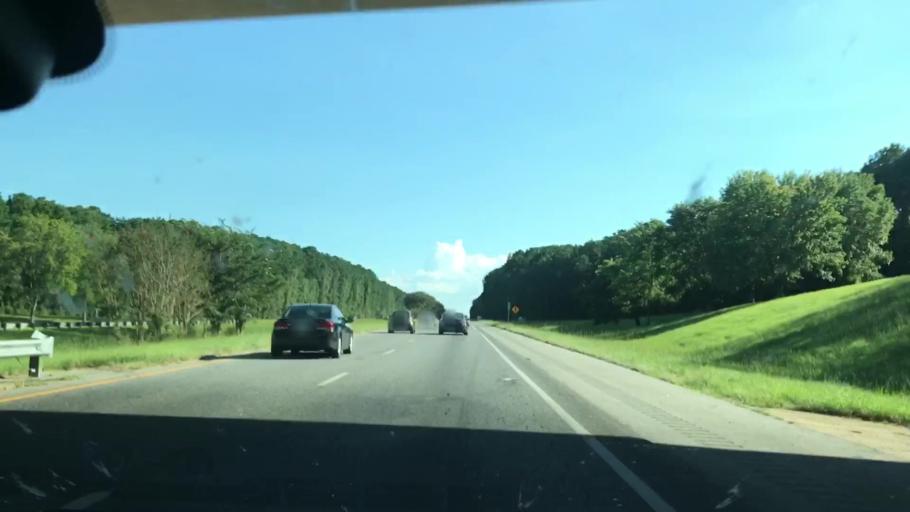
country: US
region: Georgia
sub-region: Harris County
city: Hamilton
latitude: 32.8135
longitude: -85.0213
